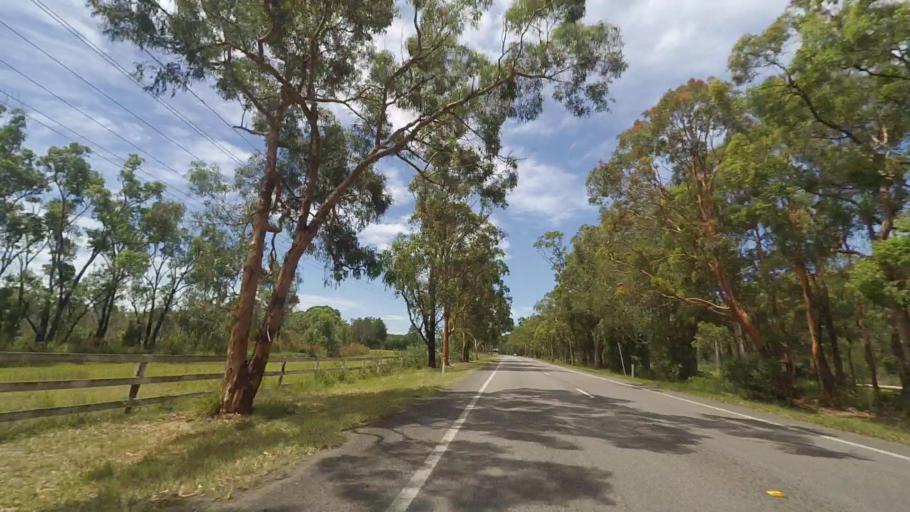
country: AU
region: New South Wales
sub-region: Port Stephens Shire
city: Medowie
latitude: -32.7679
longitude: 151.8627
